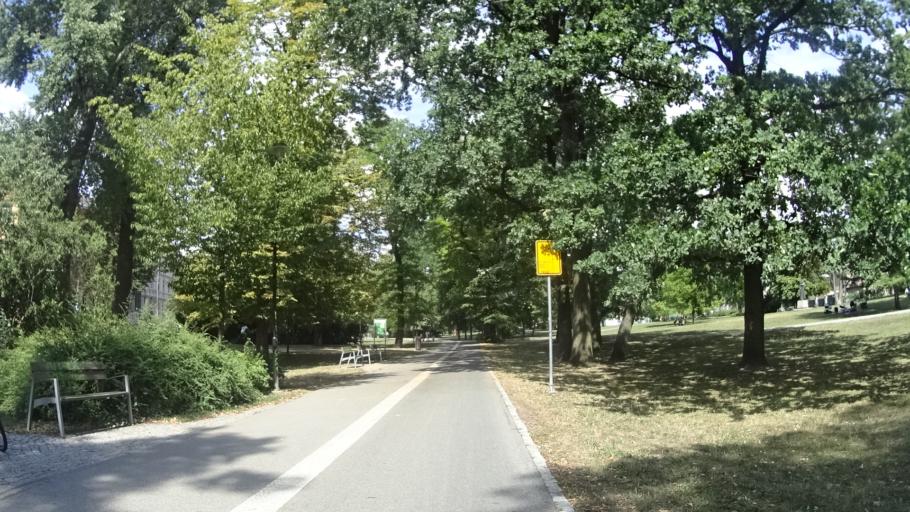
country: CZ
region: Olomoucky
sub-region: Okres Olomouc
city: Olomouc
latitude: 49.5928
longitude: 17.2444
